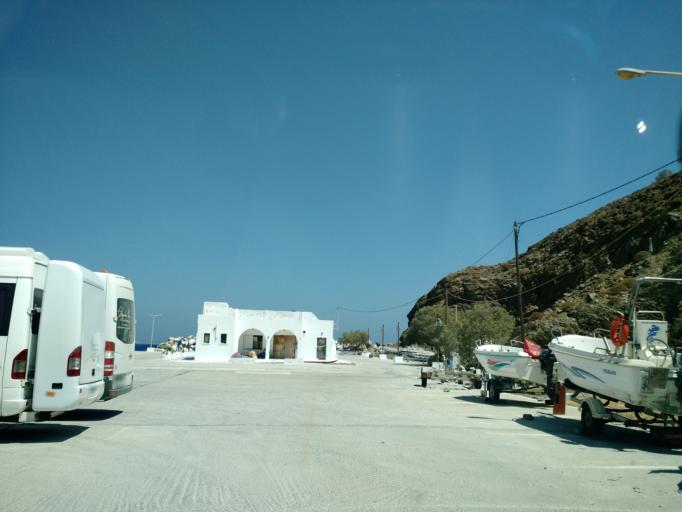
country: GR
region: South Aegean
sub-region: Nomos Dodekanisou
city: Astypalaia
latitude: 36.5470
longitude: 26.3548
